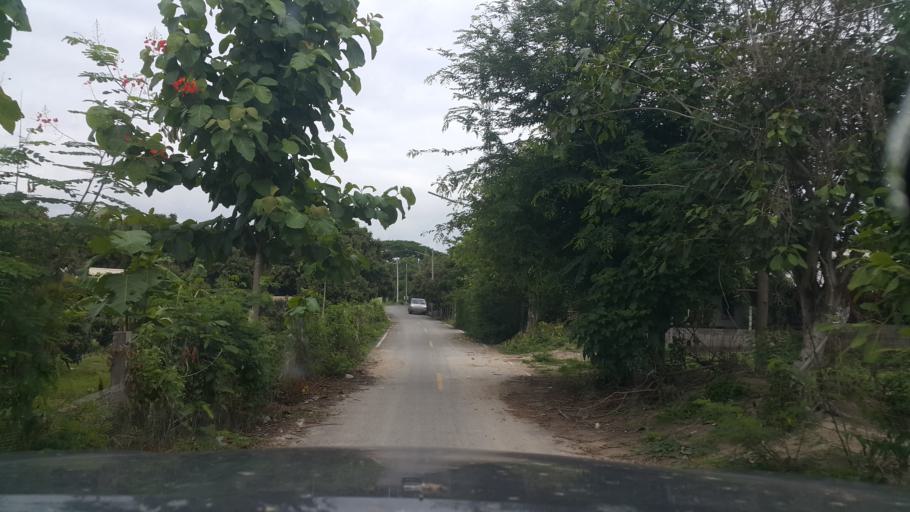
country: TH
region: Chiang Mai
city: San Pa Tong
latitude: 18.6754
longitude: 98.8294
